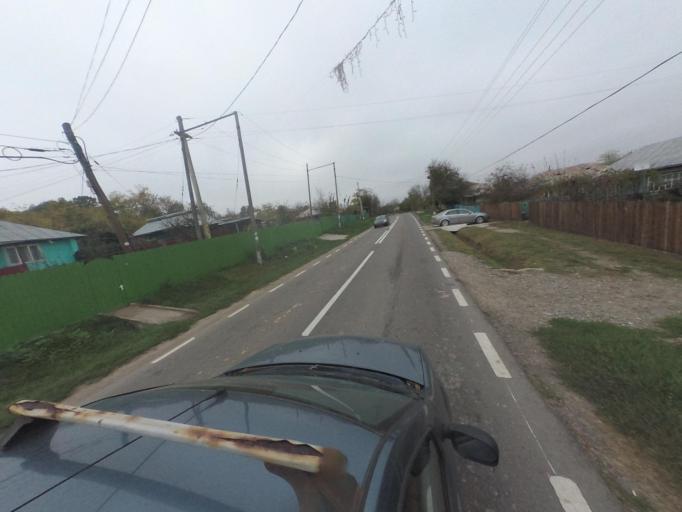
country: RO
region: Vaslui
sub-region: Comuna Bacesti
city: Bacesti
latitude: 46.8268
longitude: 27.2431
